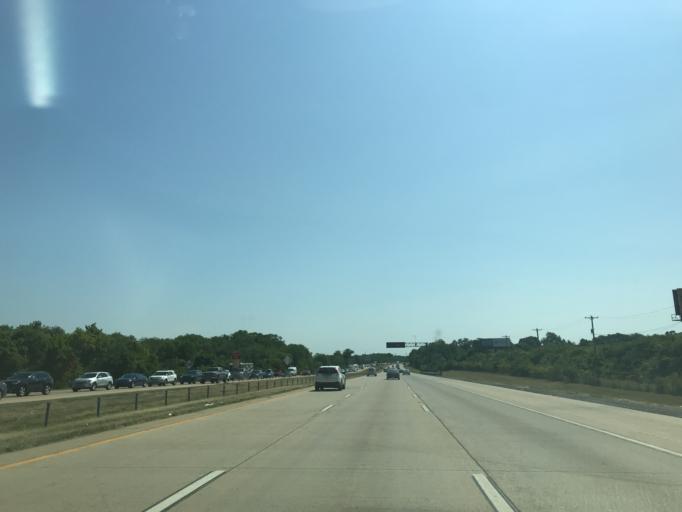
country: US
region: Delaware
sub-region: New Castle County
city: Wilmington Manor
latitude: 39.7152
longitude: -75.5762
